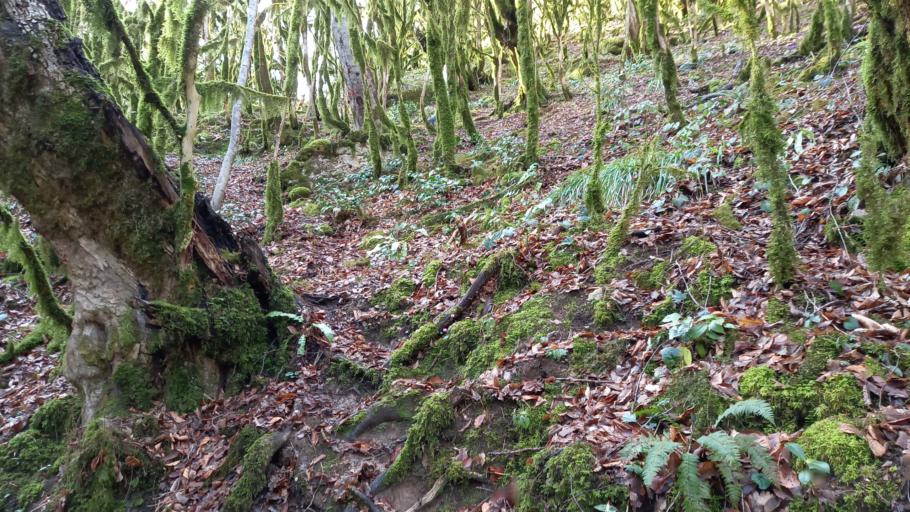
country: GE
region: Abkhazia
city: Dranda
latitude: 43.0288
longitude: 41.3325
